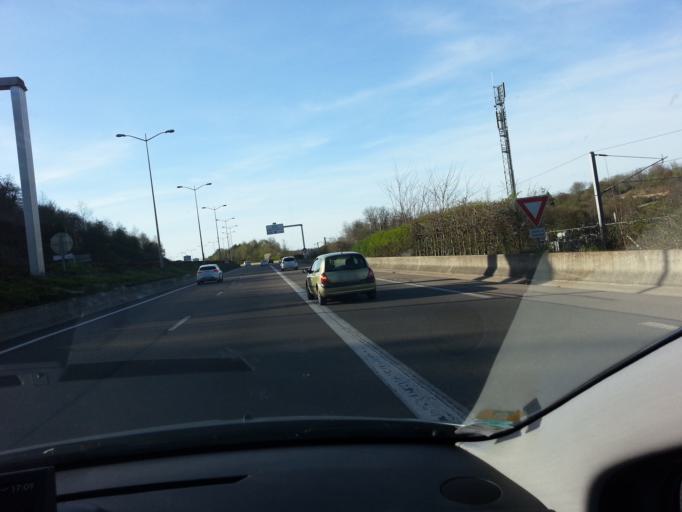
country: FR
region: Franche-Comte
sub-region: Departement du Doubs
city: Besancon
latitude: 47.2675
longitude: 6.0035
